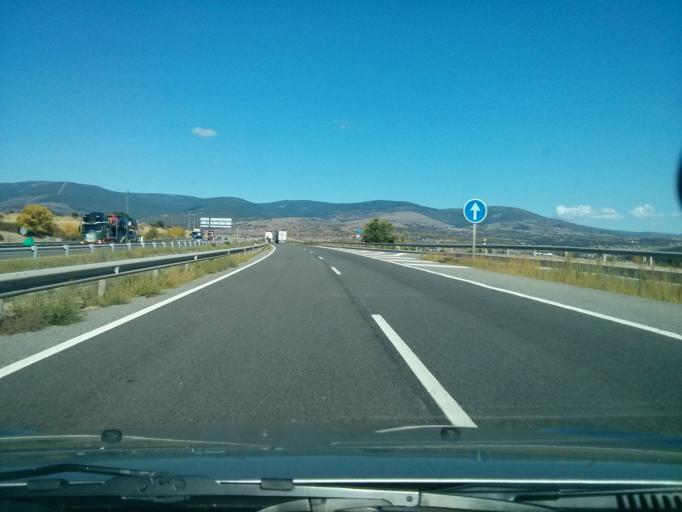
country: ES
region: Madrid
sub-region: Provincia de Madrid
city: Buitrago del Lozoya
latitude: 40.9827
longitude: -3.6391
